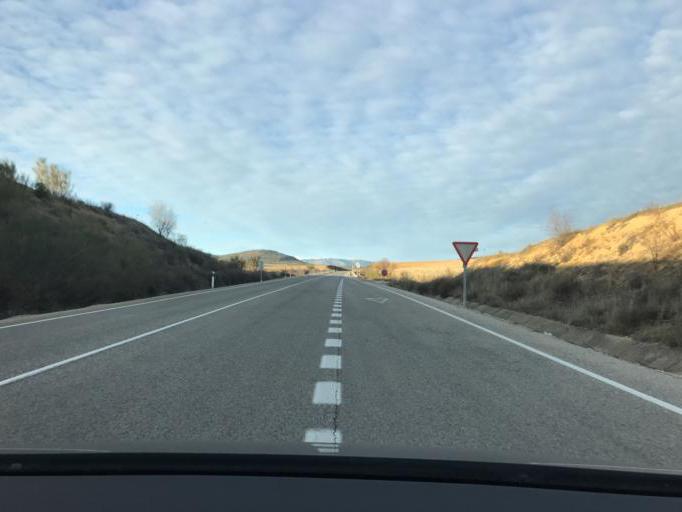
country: ES
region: Andalusia
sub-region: Provincia de Jaen
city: Guadahortuna
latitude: 37.5702
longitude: -3.4026
